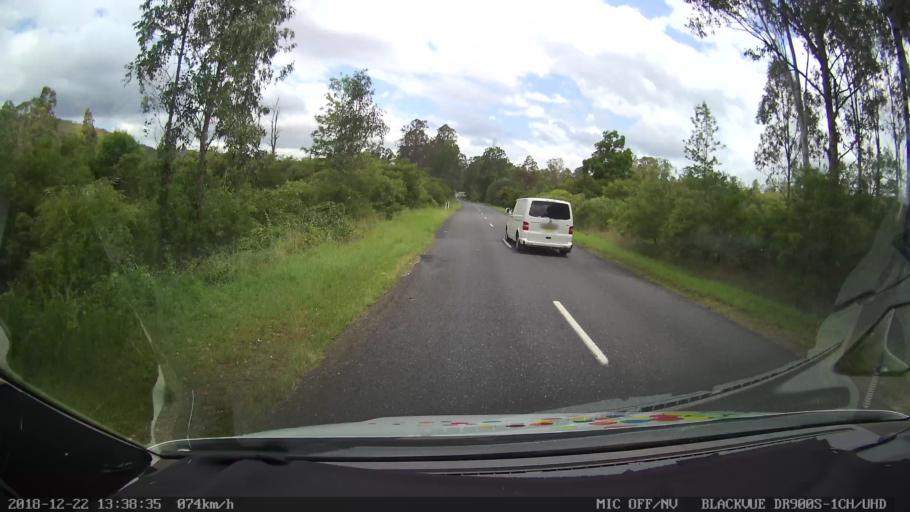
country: AU
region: New South Wales
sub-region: Clarence Valley
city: Coutts Crossing
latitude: -29.9016
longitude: 152.7862
